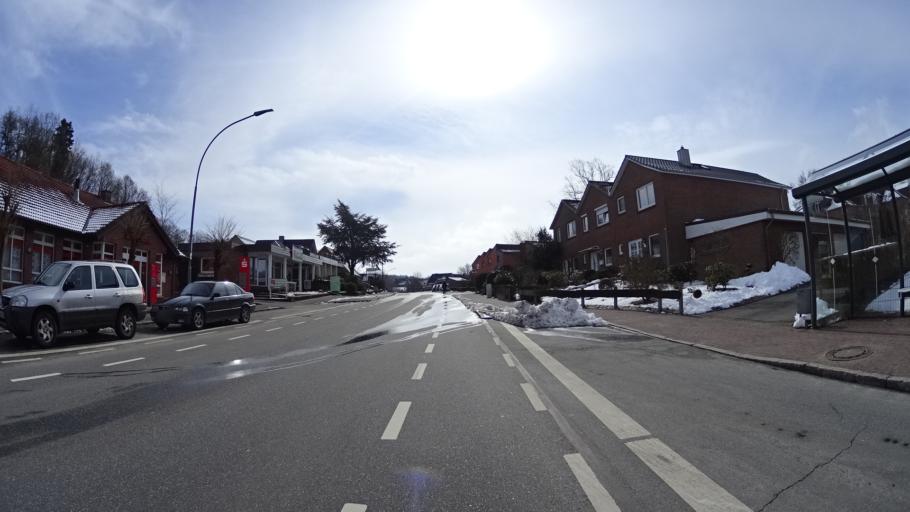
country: DE
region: Schleswig-Holstein
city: Boostedt
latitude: 54.0107
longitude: 10.0256
